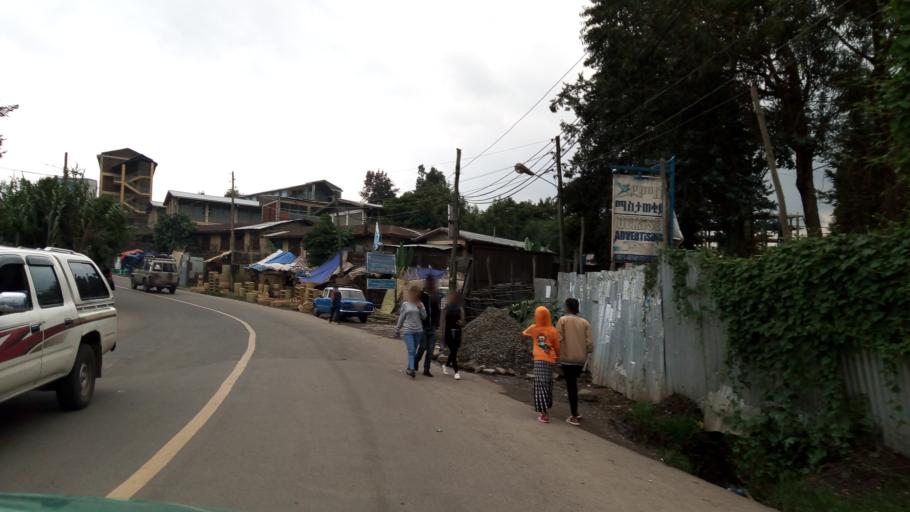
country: ET
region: Adis Abeba
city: Addis Ababa
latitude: 9.0175
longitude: 38.7740
